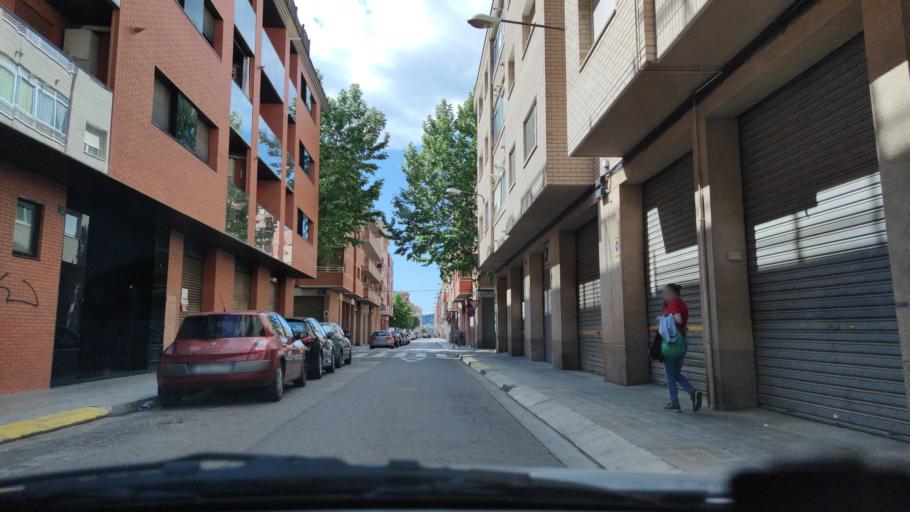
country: ES
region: Catalonia
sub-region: Provincia de Lleida
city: Lleida
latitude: 41.6049
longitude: 0.6467
